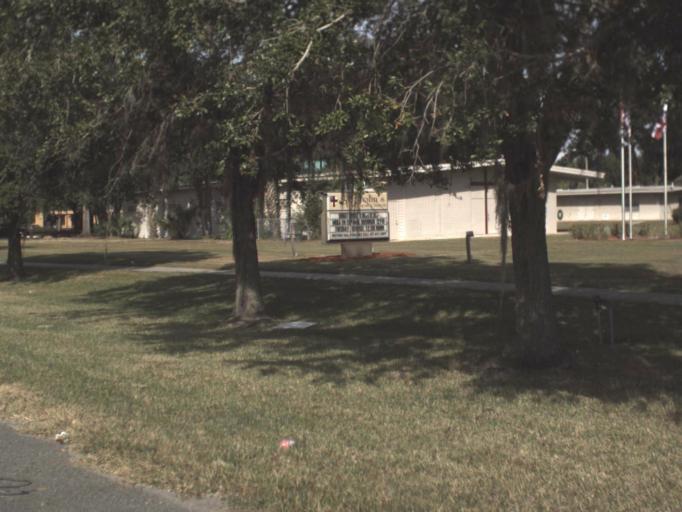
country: US
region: Florida
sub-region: Osceola County
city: Kissimmee
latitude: 28.3070
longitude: -81.4158
